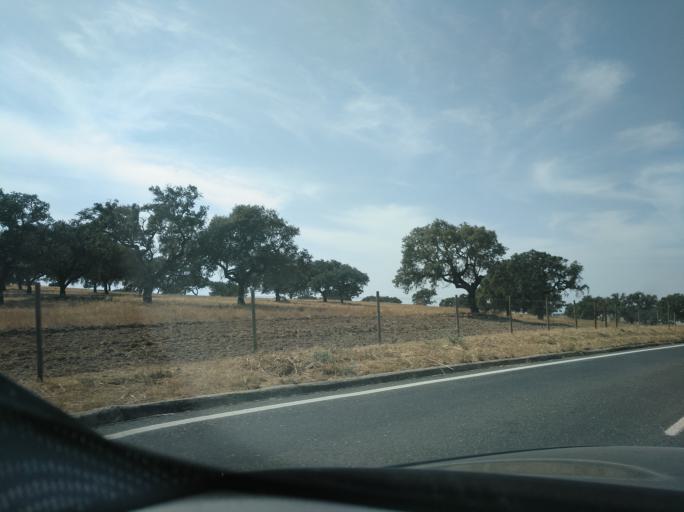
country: PT
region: Beja
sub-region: Mertola
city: Mertola
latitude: 37.7640
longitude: -7.8187
